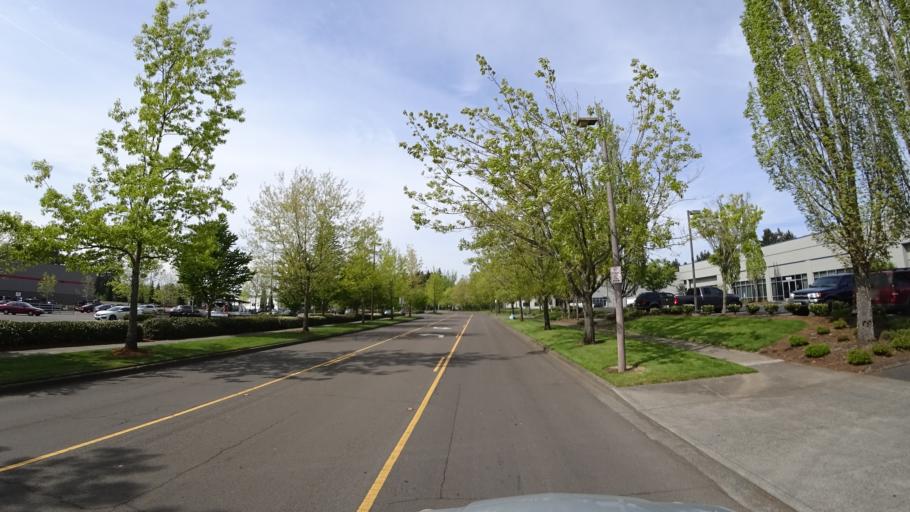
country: US
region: Oregon
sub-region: Washington County
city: Hillsboro
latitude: 45.5361
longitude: -122.9336
